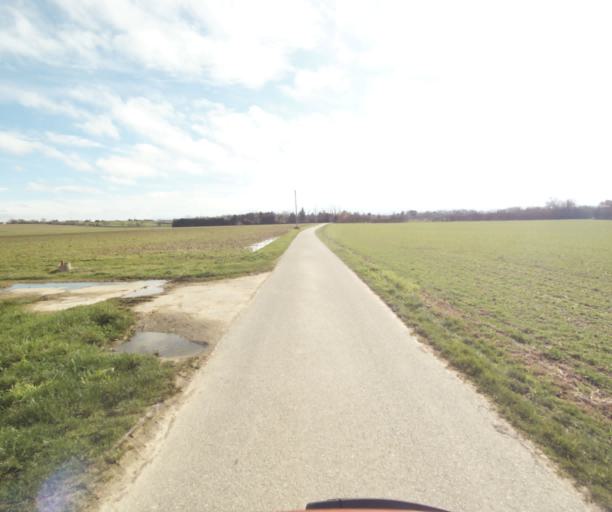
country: FR
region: Midi-Pyrenees
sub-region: Departement de l'Ariege
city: La Tour-du-Crieu
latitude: 43.1365
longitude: 1.6986
